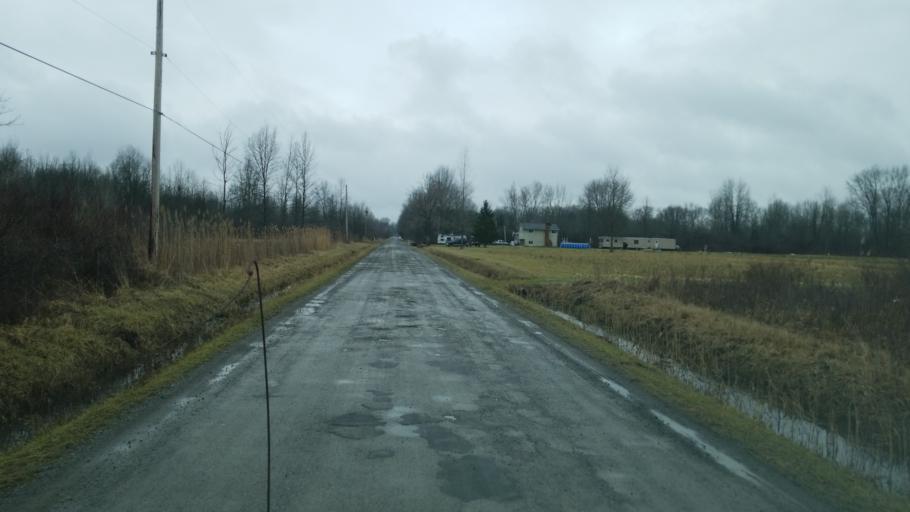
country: US
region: Ohio
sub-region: Ashtabula County
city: Orwell
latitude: 41.4558
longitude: -80.9346
